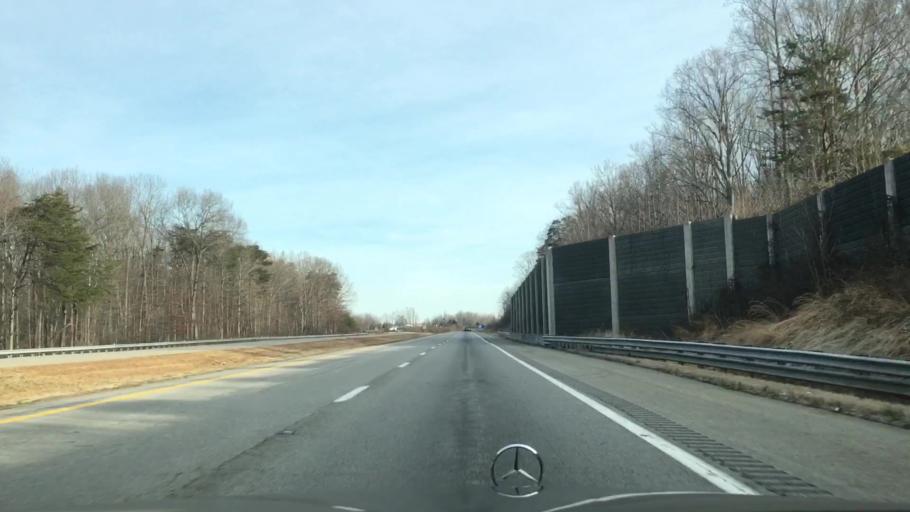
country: US
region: Virginia
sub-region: Pittsylvania County
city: Mount Hermon
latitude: 36.6786
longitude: -79.3645
